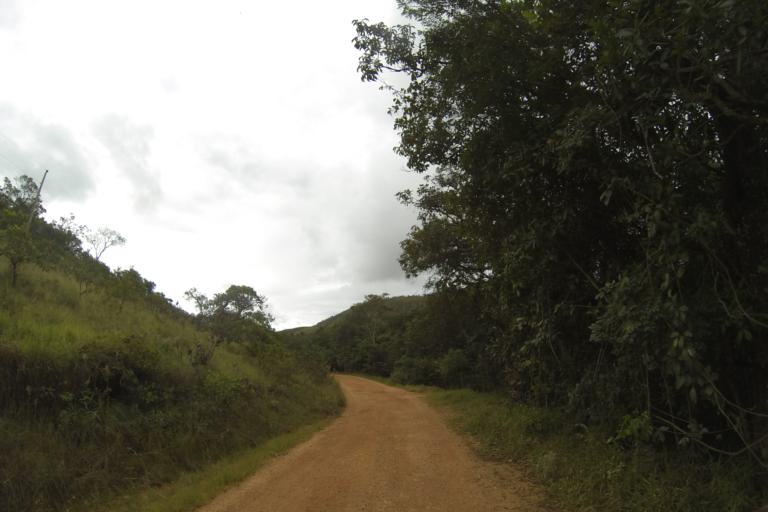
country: BR
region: Minas Gerais
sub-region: Ibia
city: Ibia
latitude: -19.7515
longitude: -46.5105
